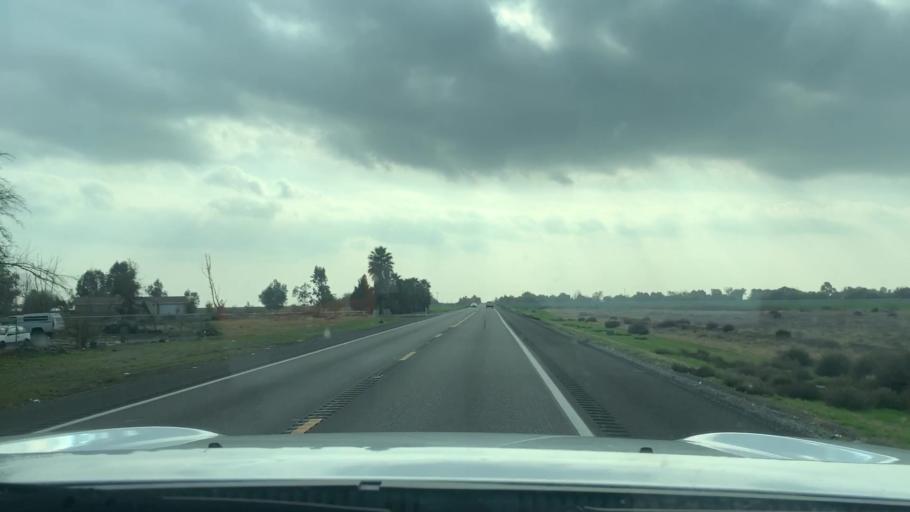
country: US
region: California
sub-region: Kings County
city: Stratford
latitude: 36.1868
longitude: -119.8299
